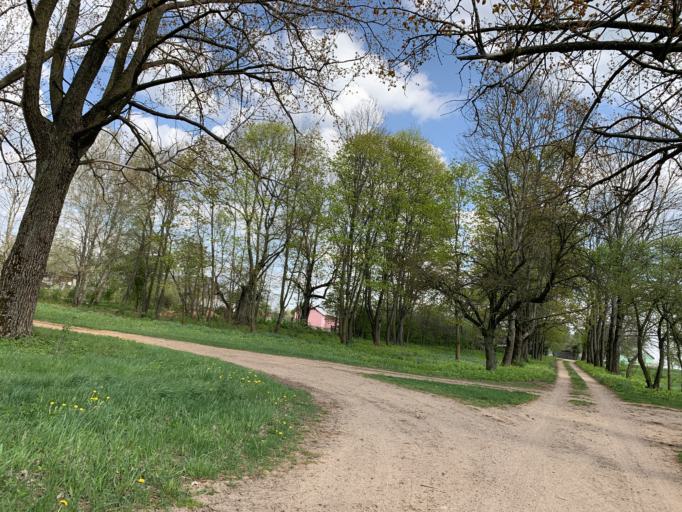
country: BY
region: Minsk
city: Nyasvizh
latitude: 53.2438
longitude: 26.6955
